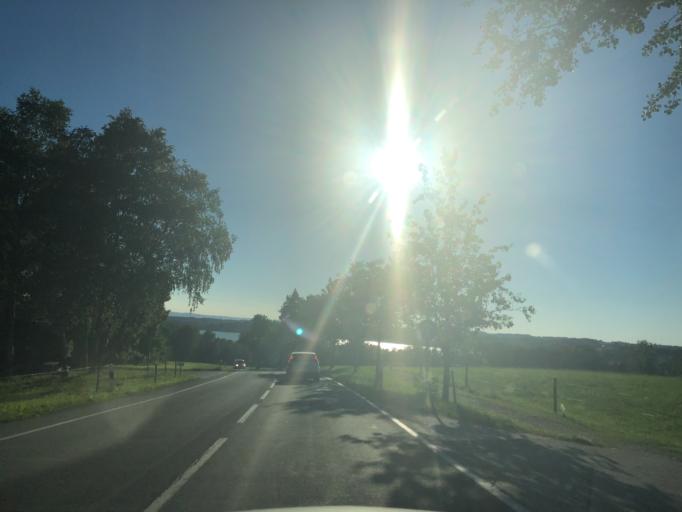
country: DE
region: Bavaria
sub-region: Upper Bavaria
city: Riedering
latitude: 47.8641
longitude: 12.2505
